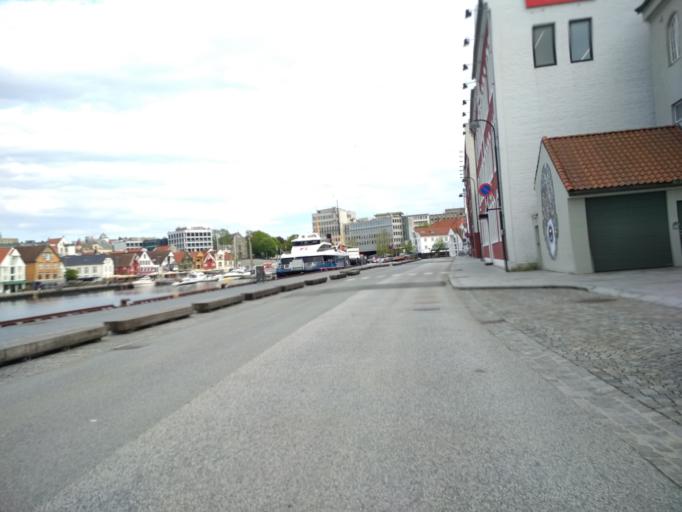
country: NO
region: Rogaland
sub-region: Stavanger
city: Stavanger
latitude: 58.9721
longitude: 5.7273
